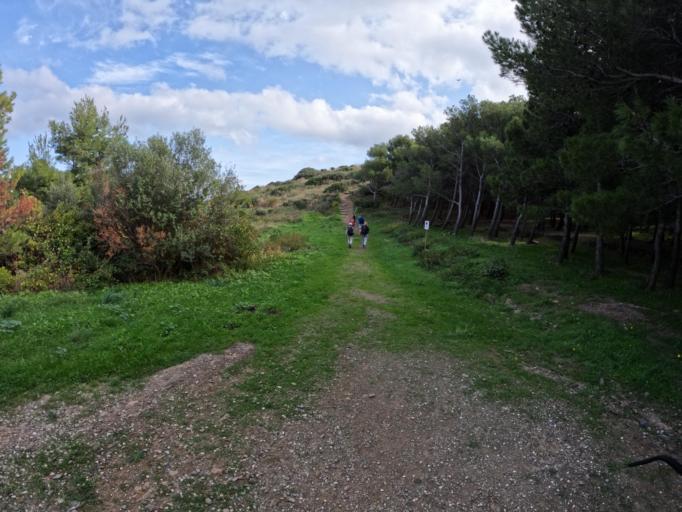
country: FR
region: Languedoc-Roussillon
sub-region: Departement des Pyrenees-Orientales
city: Cervera de la Marenda
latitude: 42.4573
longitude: 3.1619
